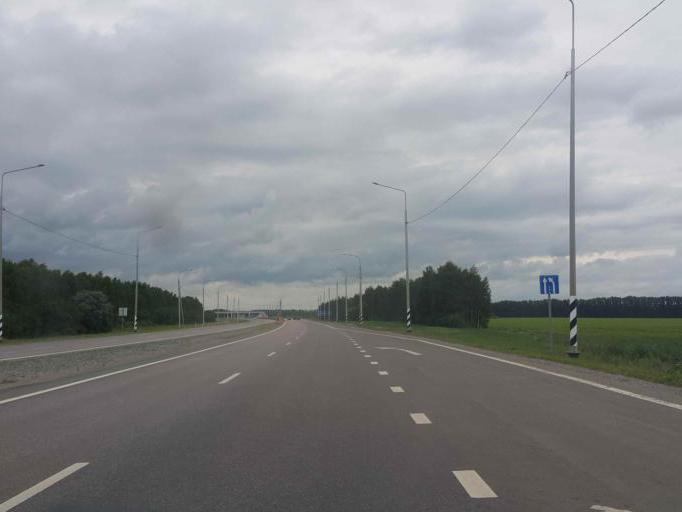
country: RU
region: Tambov
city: Zavoronezhskoye
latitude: 52.8585
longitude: 40.7715
